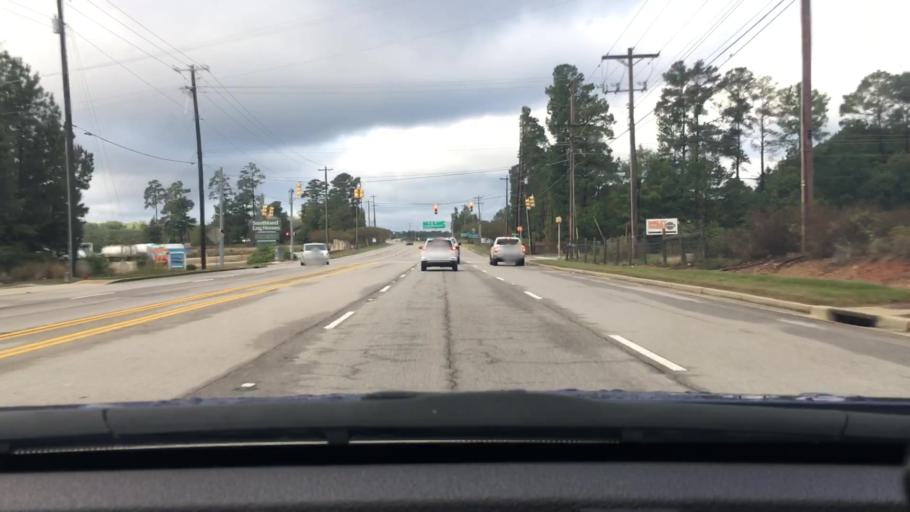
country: US
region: South Carolina
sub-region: Lexington County
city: Irmo
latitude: 34.0980
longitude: -81.1667
